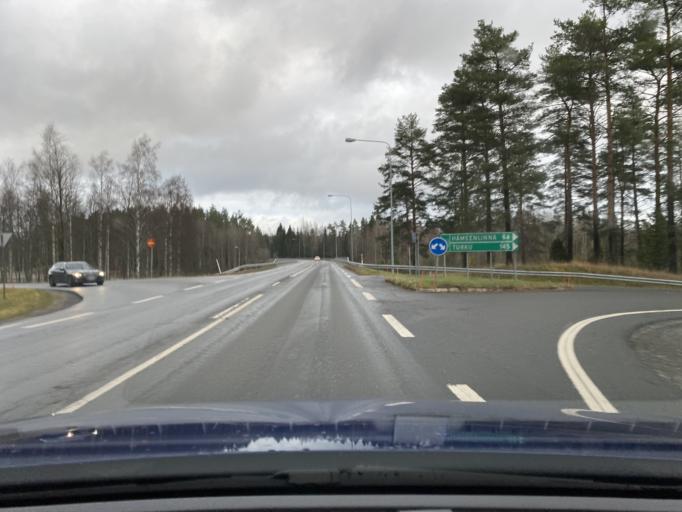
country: FI
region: Pirkanmaa
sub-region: Tampere
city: Lempaeaelae
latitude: 61.3954
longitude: 23.7820
